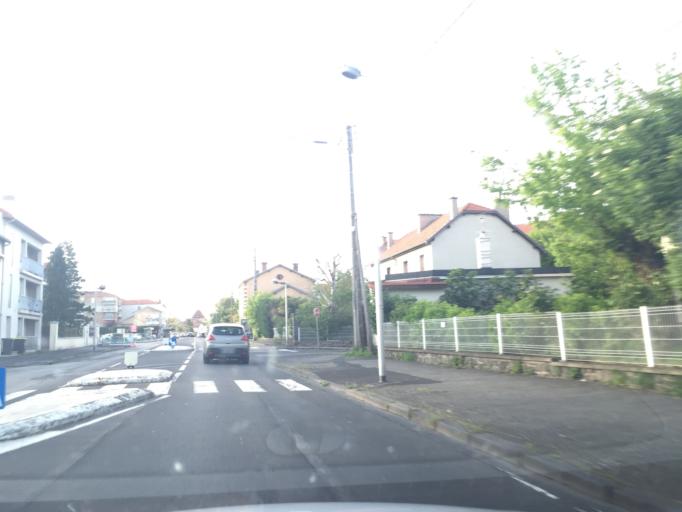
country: FR
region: Auvergne
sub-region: Departement du Puy-de-Dome
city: Riom
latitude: 45.8848
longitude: 3.1152
